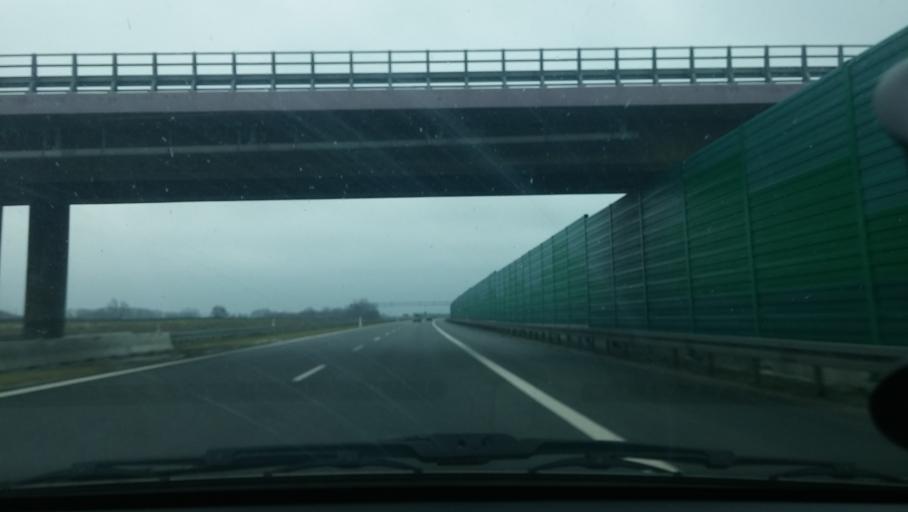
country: PL
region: Masovian Voivodeship
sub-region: Powiat minski
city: Kaluszyn
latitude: 52.2020
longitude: 21.7531
